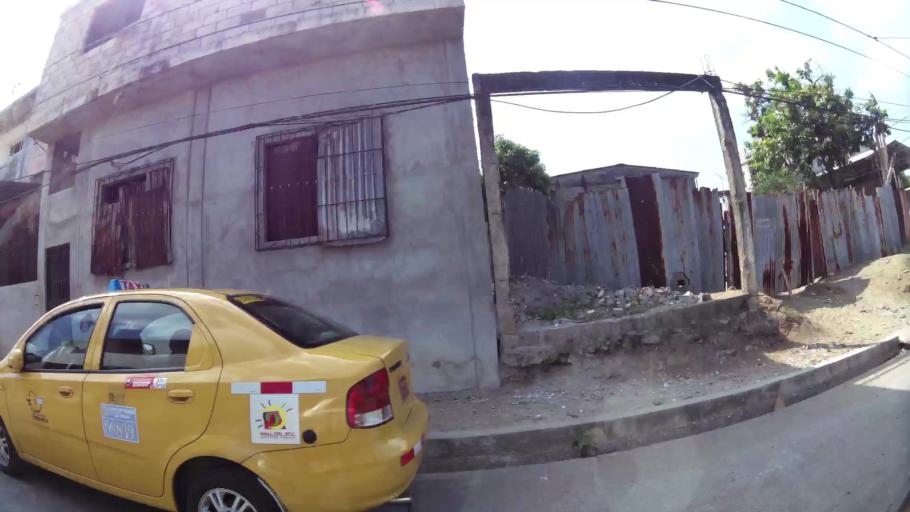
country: EC
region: Guayas
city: Santa Lucia
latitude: -2.1365
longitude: -79.9413
